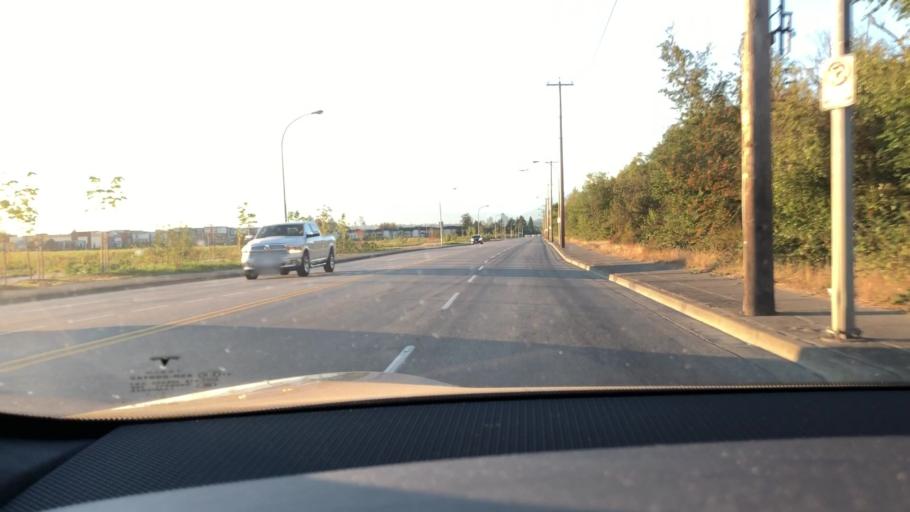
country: CA
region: British Columbia
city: Richmond
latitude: 49.1707
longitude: -123.1140
